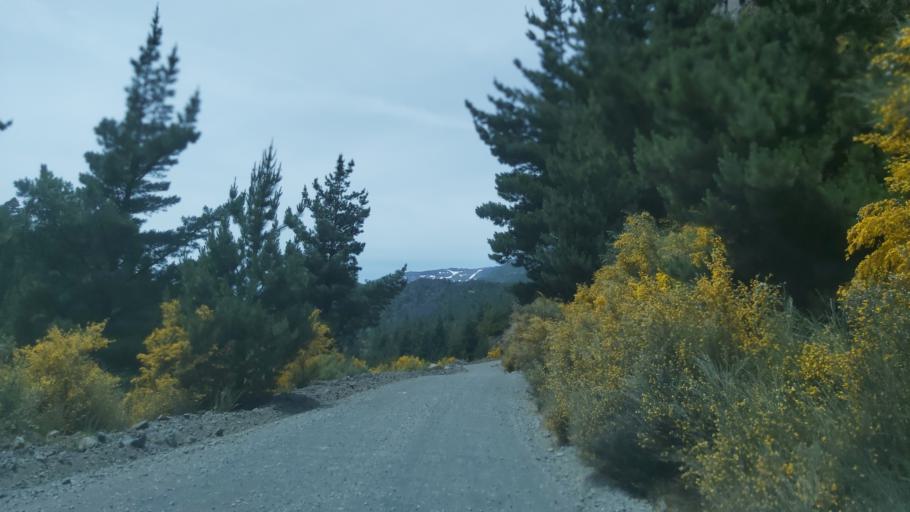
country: AR
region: Neuquen
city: Las Ovejas
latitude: -37.3924
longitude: -71.4628
